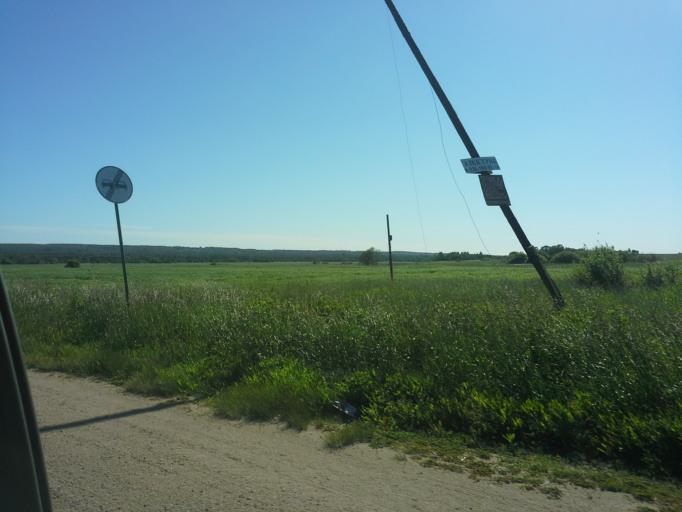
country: RU
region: Moskovskaya
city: Shemetovo
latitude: 56.5298
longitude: 38.1194
